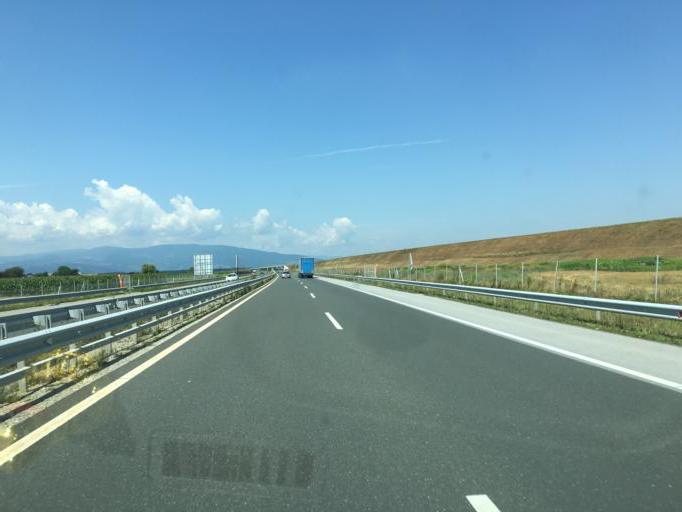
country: SI
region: Starse
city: Starse
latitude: 46.4480
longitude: 15.7697
